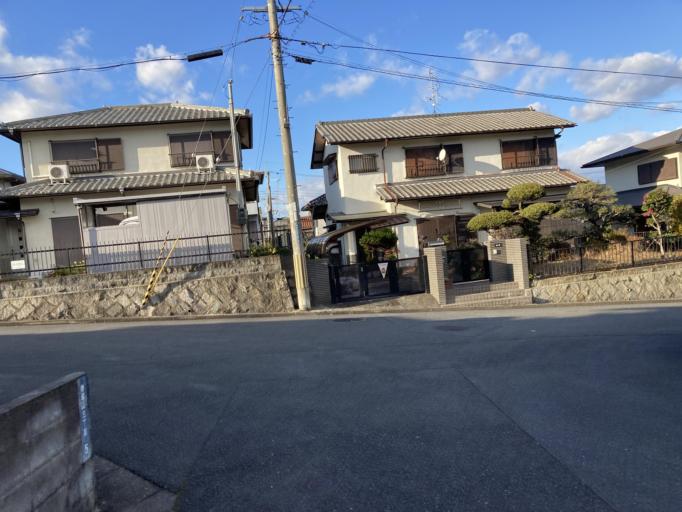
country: JP
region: Nara
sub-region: Ikoma-shi
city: Ikoma
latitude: 34.6832
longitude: 135.7272
